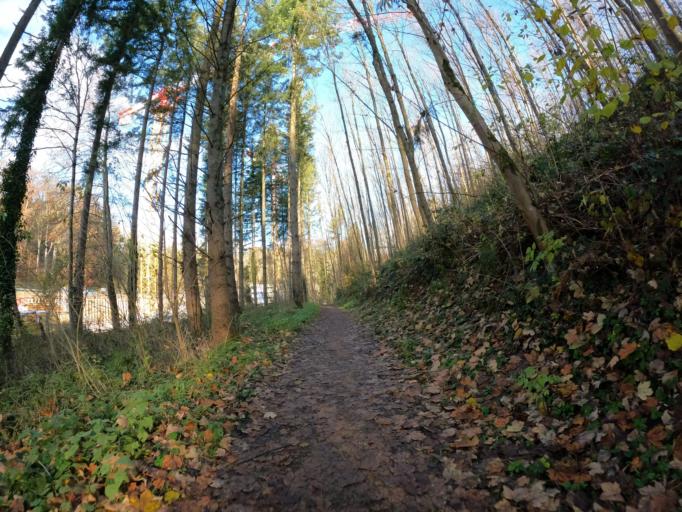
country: LU
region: Luxembourg
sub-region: Canton de Luxembourg
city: Bertrange
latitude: 49.6254
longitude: 6.0417
